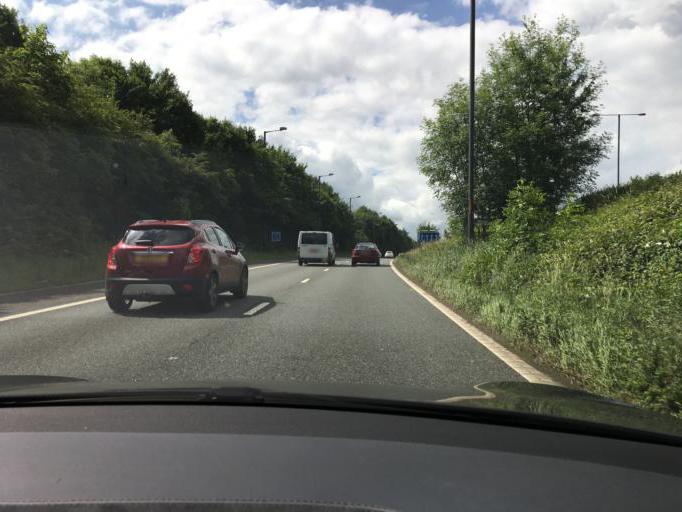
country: GB
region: England
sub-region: Manchester
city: Chorlton cum Hardy
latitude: 53.3955
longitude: -2.2687
